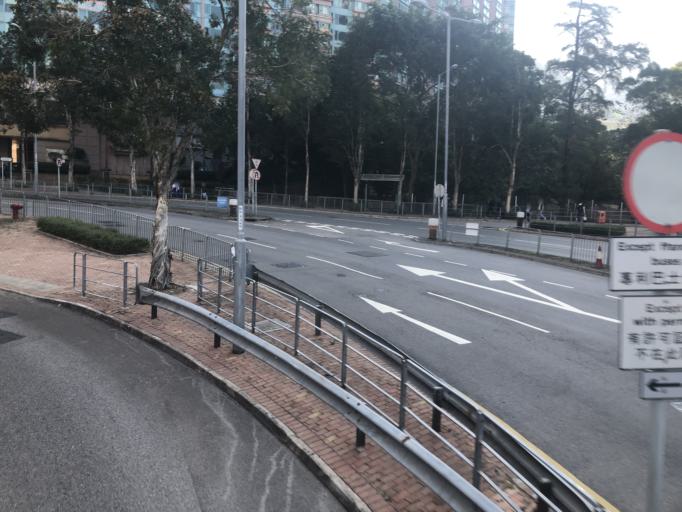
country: HK
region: Sai Kung
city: Sai Kung
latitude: 22.4279
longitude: 114.2427
